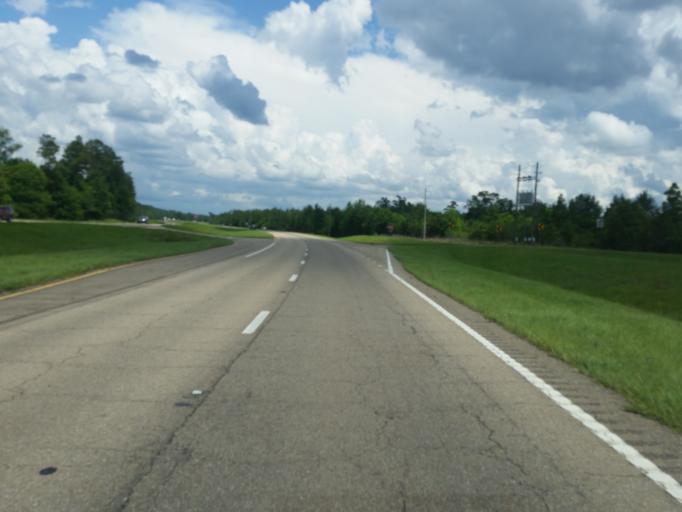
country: US
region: Mississippi
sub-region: Perry County
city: New Augusta
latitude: 31.1452
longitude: -88.8807
